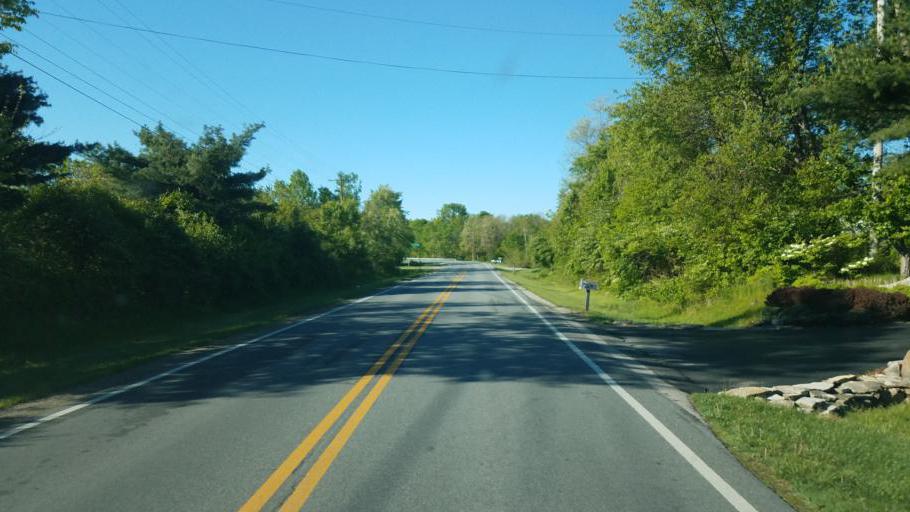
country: US
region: Ohio
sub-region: Delaware County
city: Sunbury
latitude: 40.1925
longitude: -82.8724
